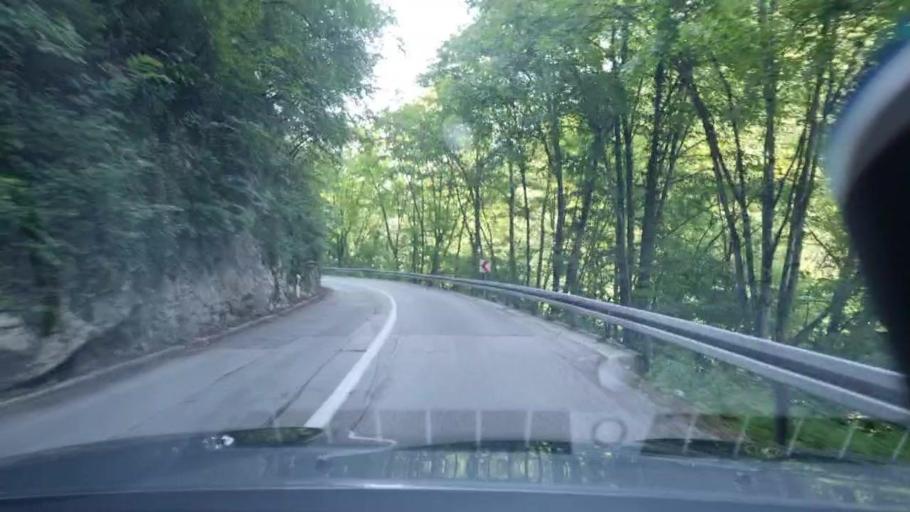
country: BA
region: Federation of Bosnia and Herzegovina
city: Bosanska Krupa
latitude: 44.8739
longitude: 16.0774
